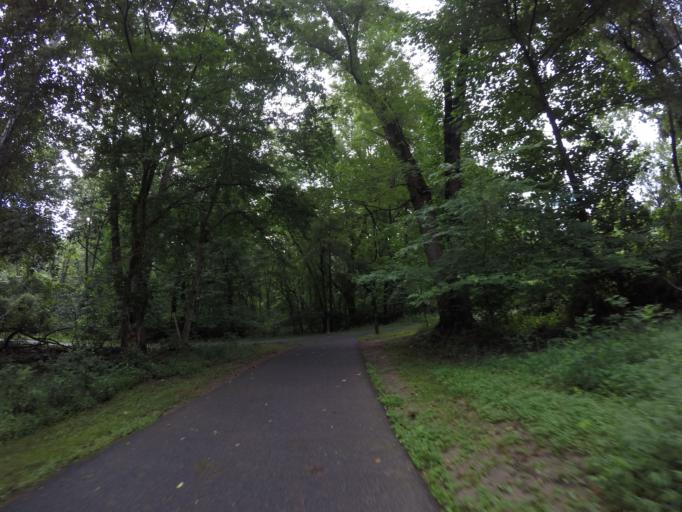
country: US
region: Maryland
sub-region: Prince George's County
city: Berwyn Heights
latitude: 38.9819
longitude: -76.9205
